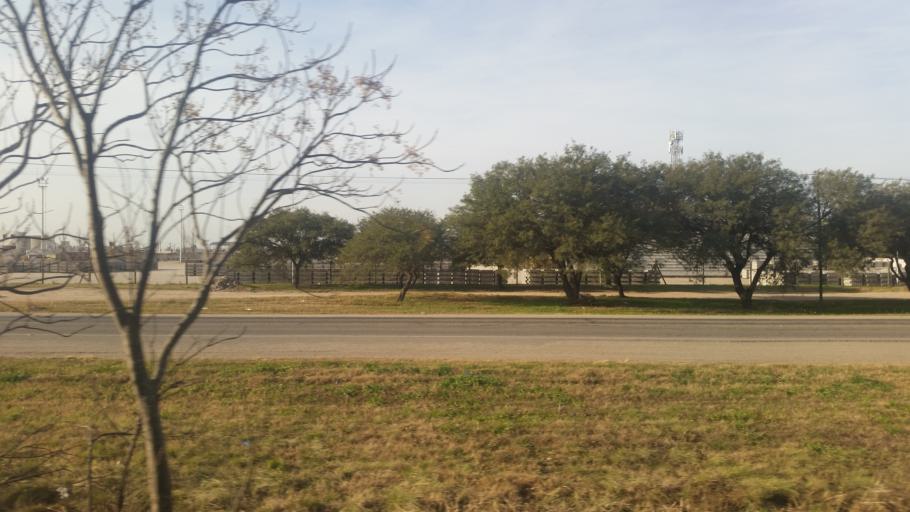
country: AR
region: Cordoba
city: Toledo
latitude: -31.5630
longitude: -64.0025
